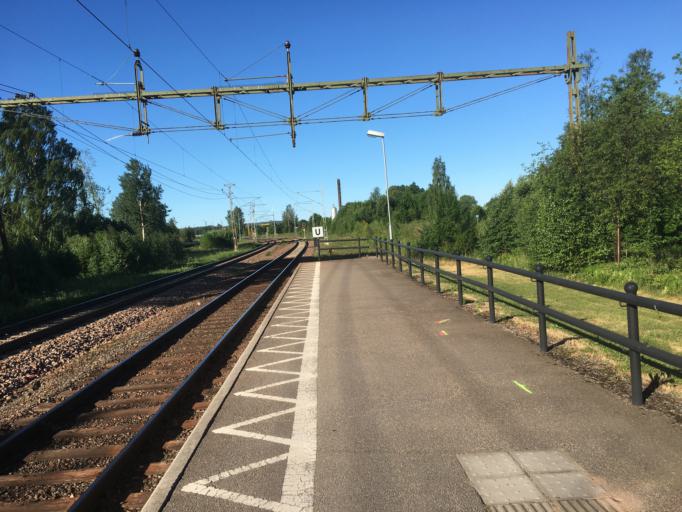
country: SE
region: Gaevleborg
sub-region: Hofors Kommun
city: Hofors
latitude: 60.5133
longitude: 16.4881
